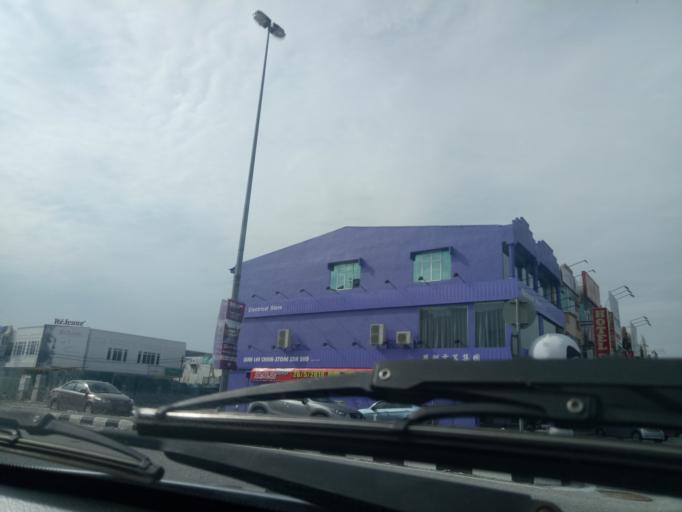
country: MY
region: Perak
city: Ipoh
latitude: 4.6189
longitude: 101.1167
